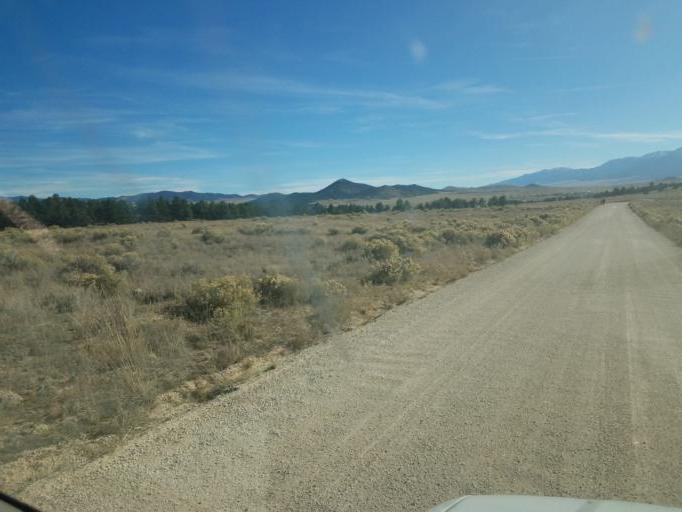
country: US
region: Colorado
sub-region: Custer County
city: Westcliffe
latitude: 38.2292
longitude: -105.4573
